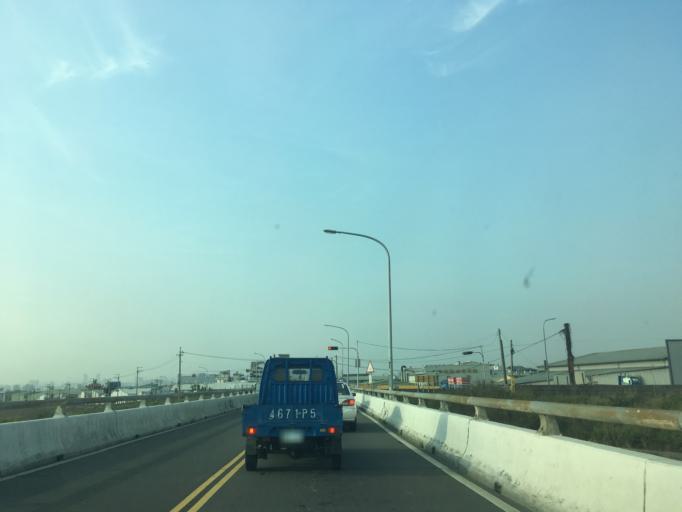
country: TW
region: Taiwan
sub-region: Taichung City
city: Taichung
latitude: 24.0734
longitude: 120.6800
